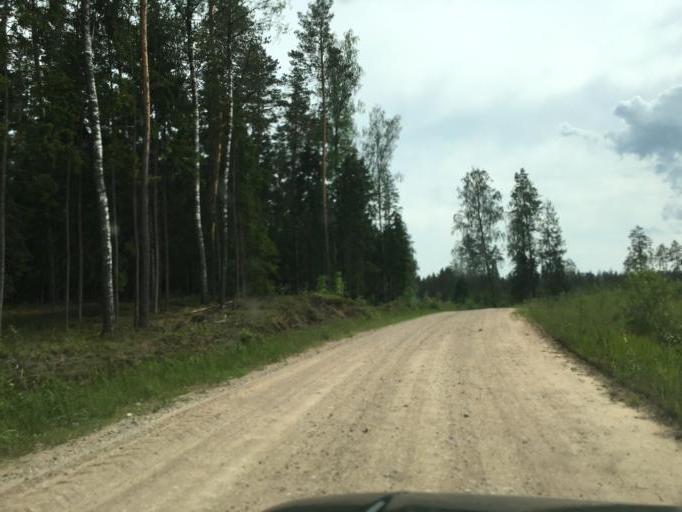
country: LV
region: Rugaju
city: Rugaji
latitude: 56.7739
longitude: 27.1047
